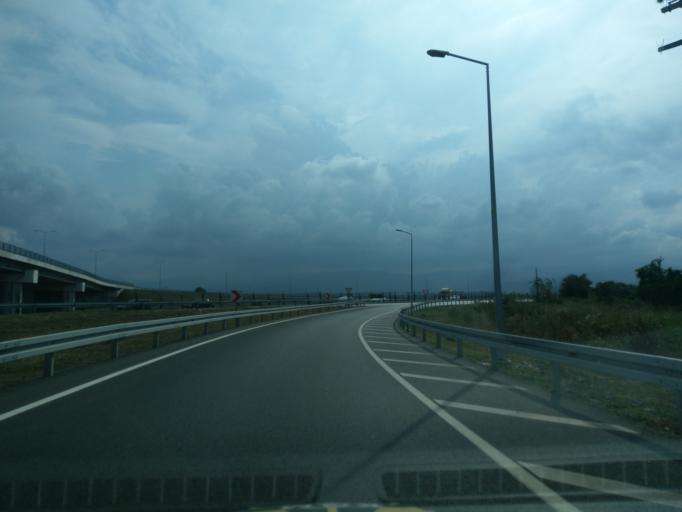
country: TR
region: Samsun
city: Tekkekoy
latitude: 41.2374
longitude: 36.5356
